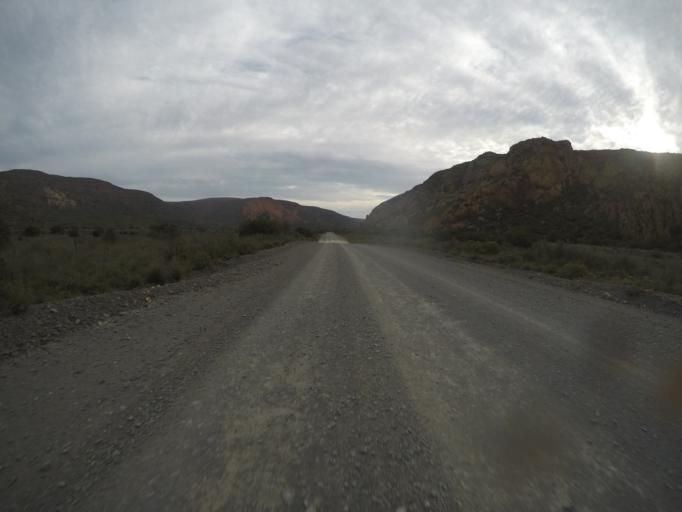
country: ZA
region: Eastern Cape
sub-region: Cacadu District Municipality
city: Willowmore
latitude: -33.5211
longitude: 23.6620
